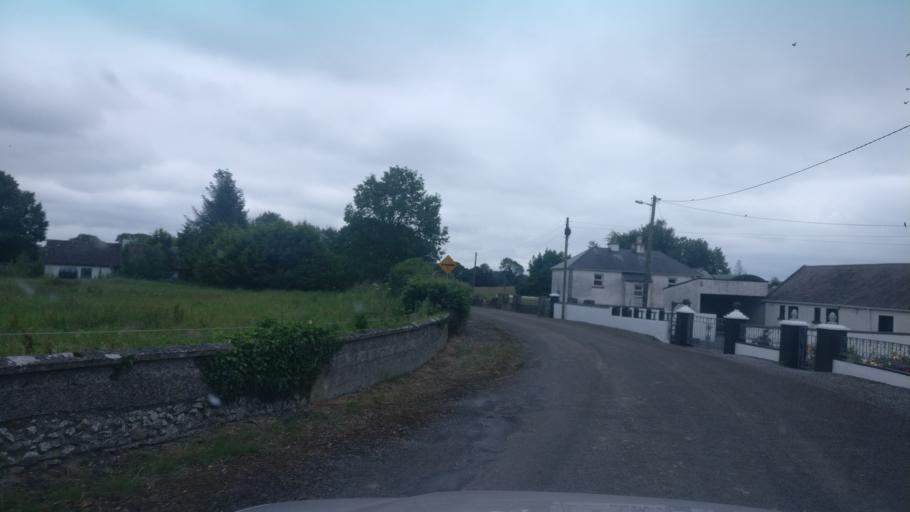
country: IE
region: Connaught
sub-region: County Galway
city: Ballinasloe
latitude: 53.2909
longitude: -8.3393
